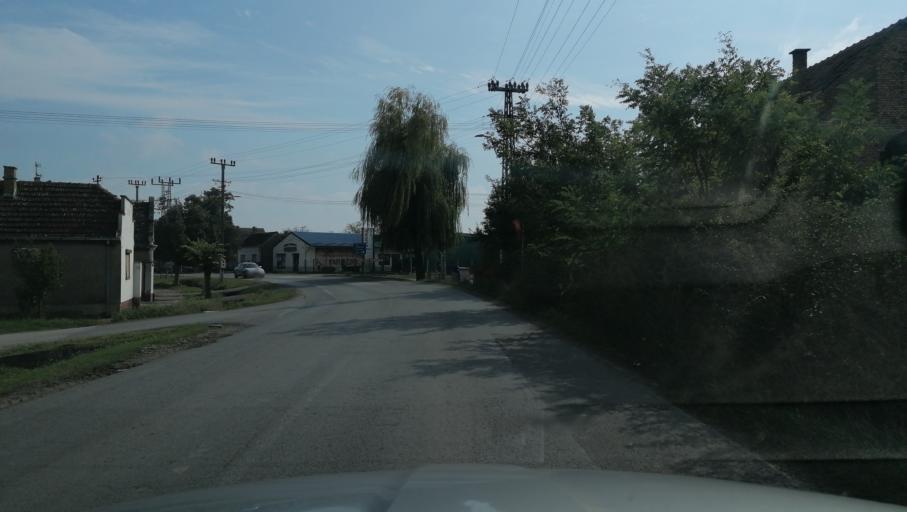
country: RS
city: Ravnje
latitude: 45.0251
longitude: 19.3965
